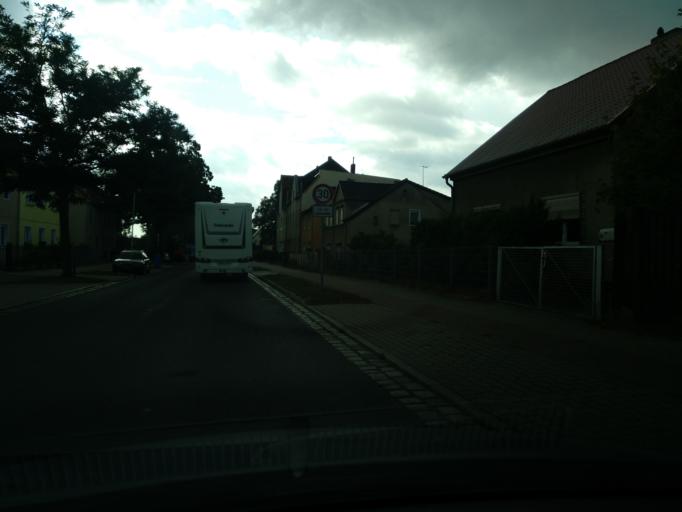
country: DE
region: Brandenburg
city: Woltersdorf
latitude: 52.4824
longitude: 13.7760
